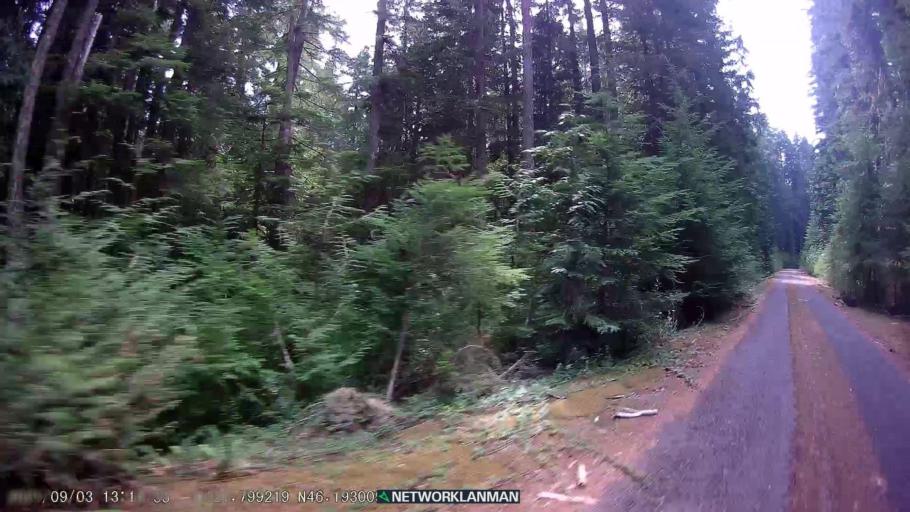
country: US
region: Washington
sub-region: Skamania County
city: Carson
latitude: 46.1929
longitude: -121.7993
